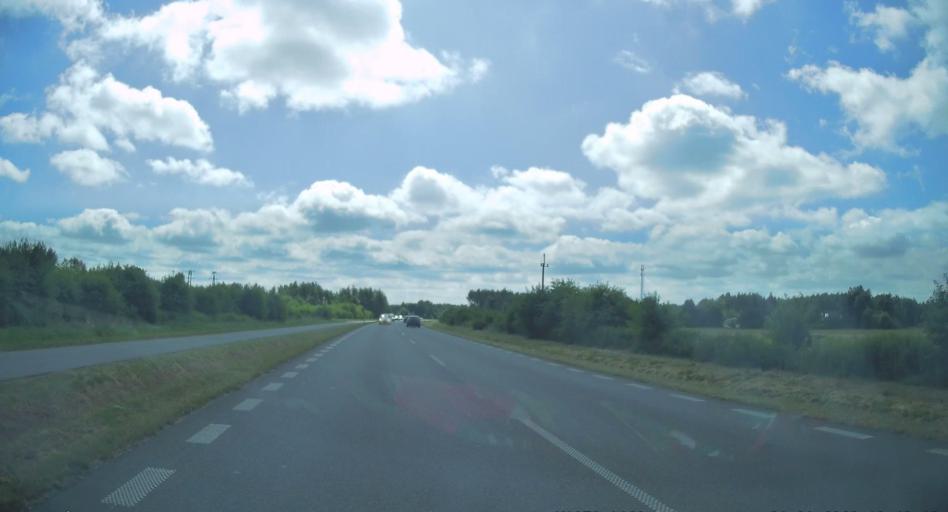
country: PL
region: Subcarpathian Voivodeship
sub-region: Powiat mielecki
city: Padew Narodowa
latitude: 50.3700
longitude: 21.4820
